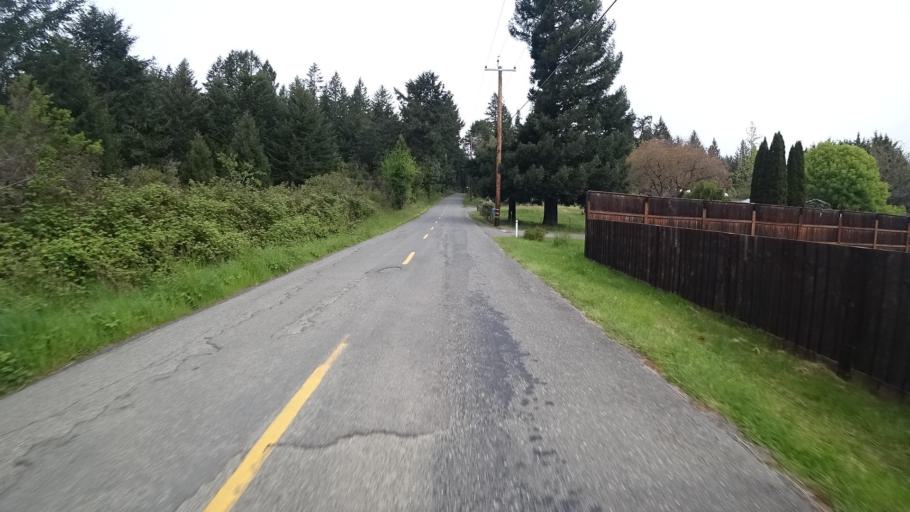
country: US
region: California
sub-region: Humboldt County
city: Redway
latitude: 40.2980
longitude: -123.8213
